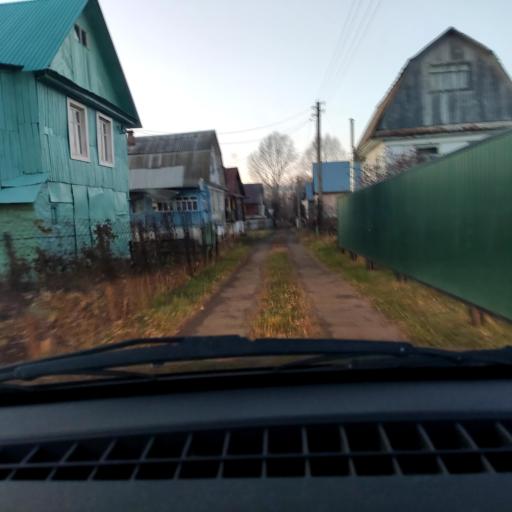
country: RU
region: Bashkortostan
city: Ufa
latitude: 54.6497
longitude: 55.8985
